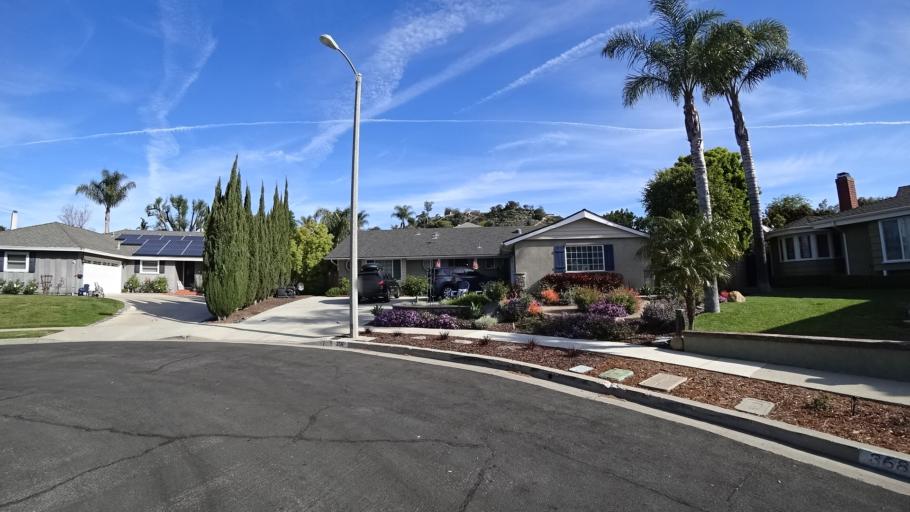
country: US
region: California
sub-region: Ventura County
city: Casa Conejo
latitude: 34.1717
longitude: -118.9622
